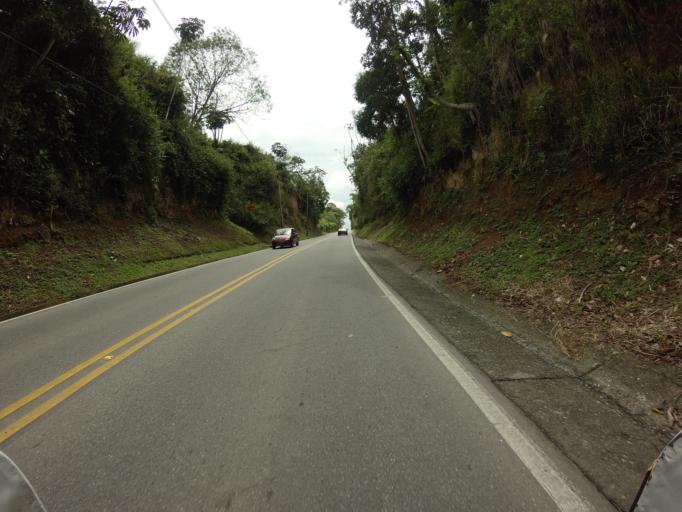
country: CO
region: Quindio
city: Quimbaya
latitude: 4.6002
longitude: -75.7790
